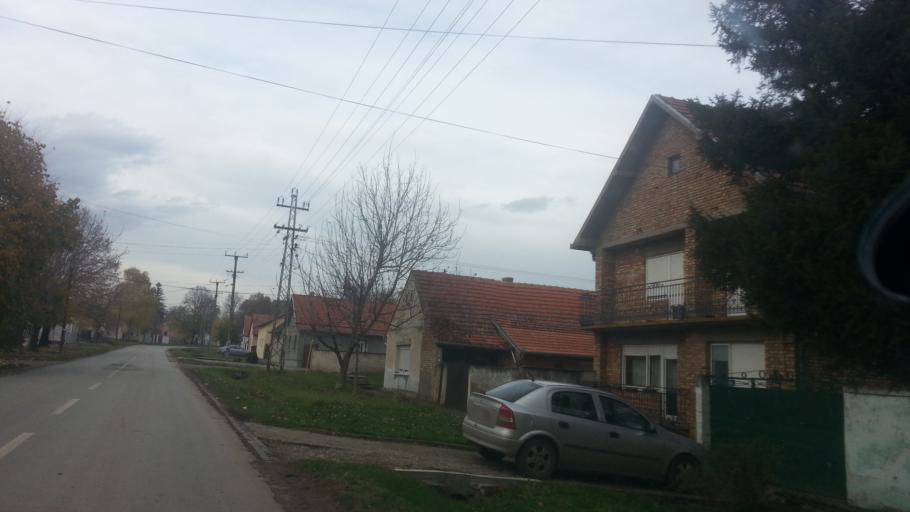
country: RS
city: Putinci
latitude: 44.9855
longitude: 19.9684
